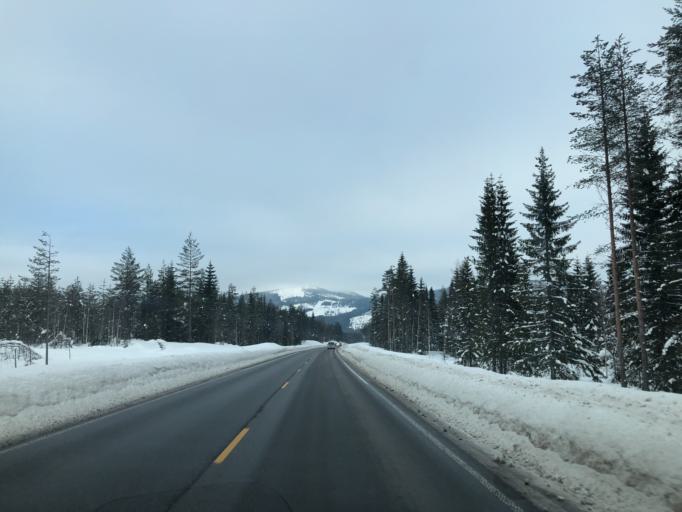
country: NO
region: Hedmark
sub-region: Trysil
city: Innbygda
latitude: 61.2526
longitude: 12.2992
